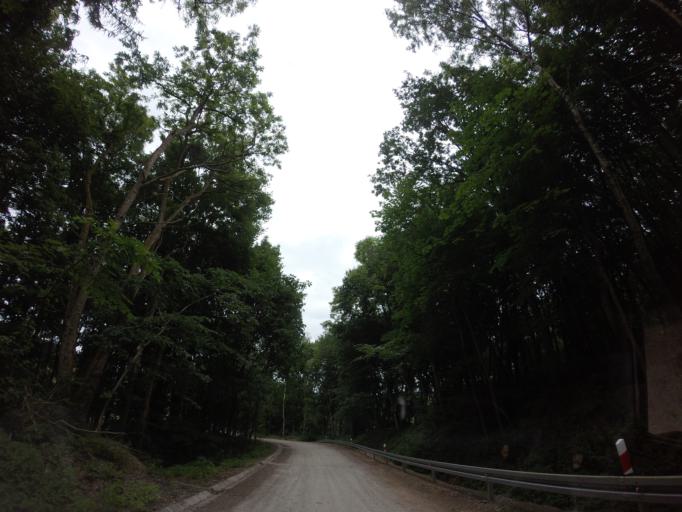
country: PL
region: Lubusz
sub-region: Powiat strzelecko-drezdenecki
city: Stare Kurowo
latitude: 52.9031
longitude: 15.6621
